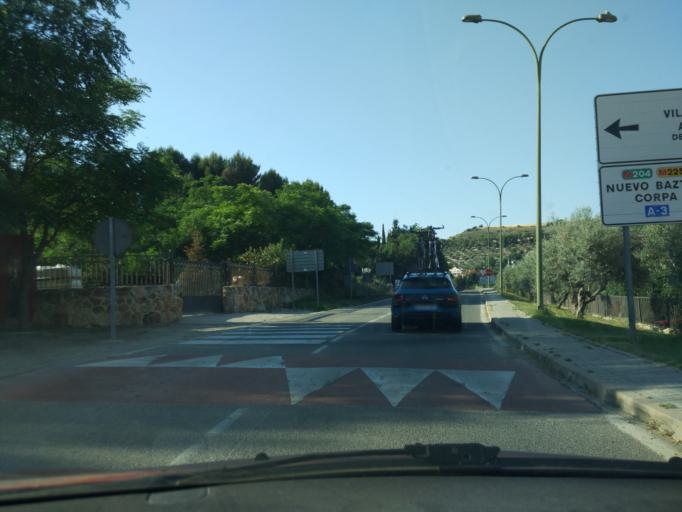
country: ES
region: Madrid
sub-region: Provincia de Madrid
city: Valverde de Alcala
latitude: 40.4177
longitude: -3.2994
